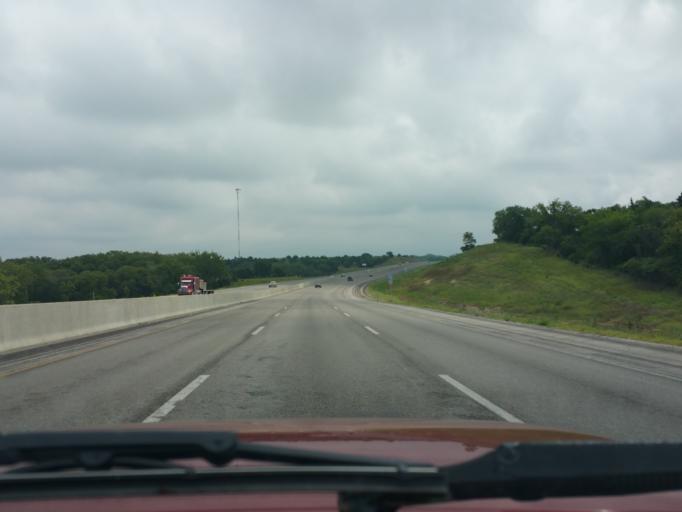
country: US
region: Kansas
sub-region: Shawnee County
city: Topeka
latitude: 39.0179
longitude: -95.4962
